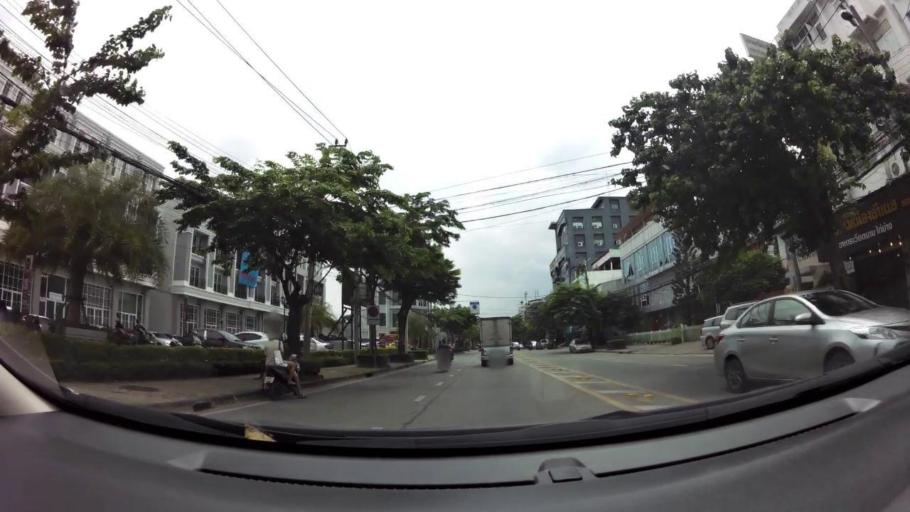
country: TH
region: Bangkok
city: Bang Na
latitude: 13.6783
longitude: 100.6248
